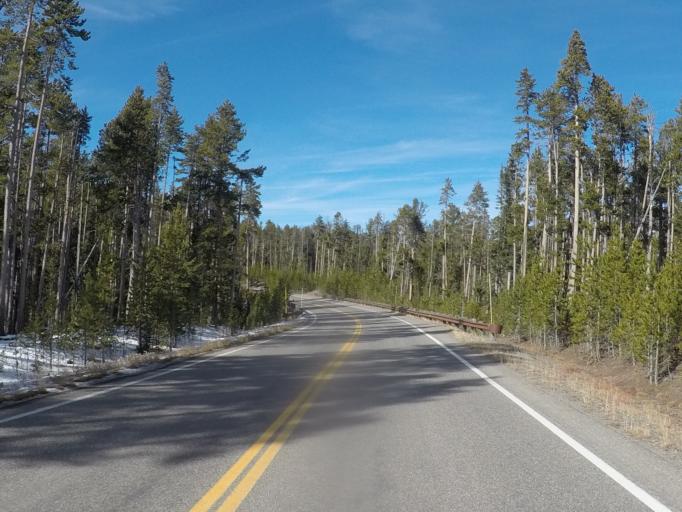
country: US
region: Montana
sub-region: Gallatin County
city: West Yellowstone
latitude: 44.4312
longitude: -110.6586
